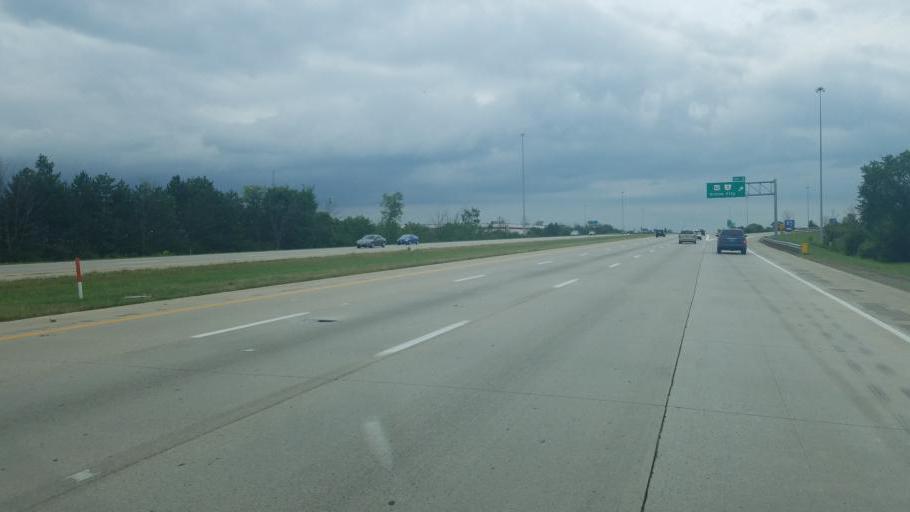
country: US
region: Ohio
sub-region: Franklin County
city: Grove City
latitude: 39.9051
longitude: -83.0833
